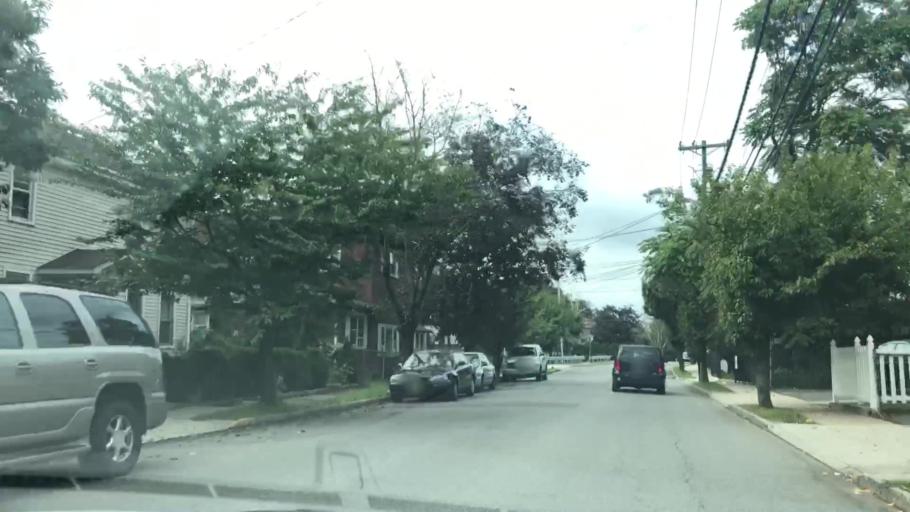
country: US
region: New Jersey
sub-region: Essex County
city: Bloomfield
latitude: 40.7915
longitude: -74.1770
